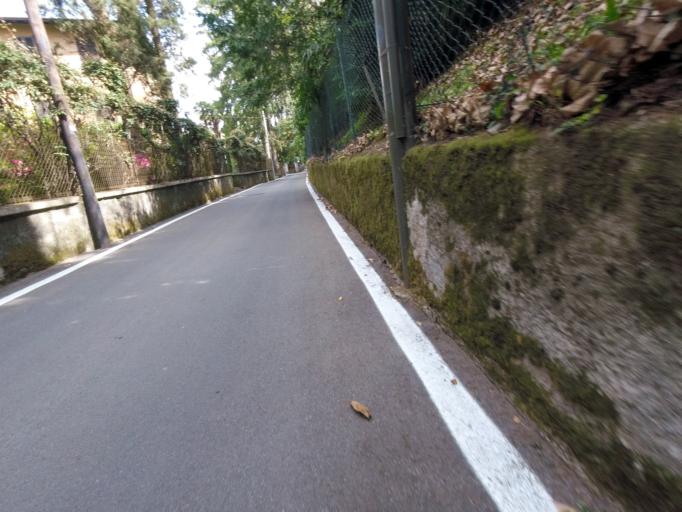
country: IT
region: Lombardy
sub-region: Provincia di Como
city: Cadenabbia
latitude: 45.9905
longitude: 9.2339
